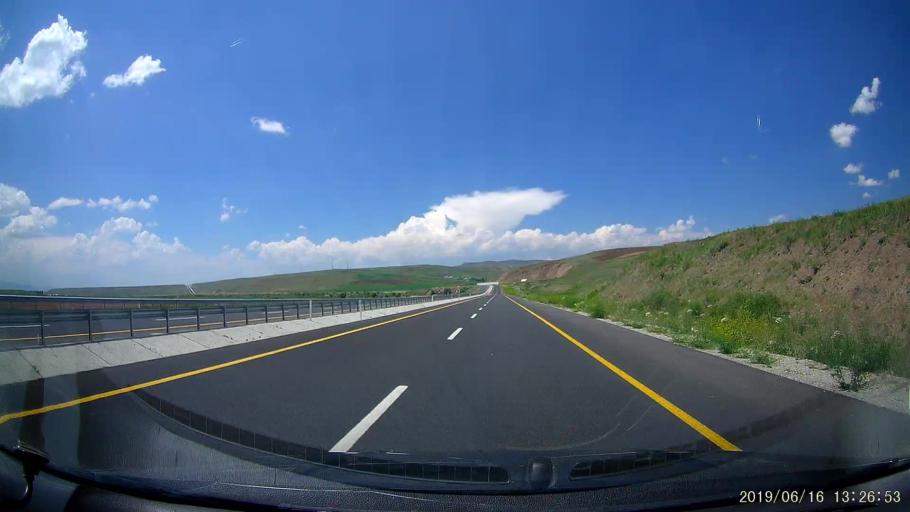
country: TR
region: Agri
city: Taslicay
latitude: 39.6634
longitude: 43.3189
